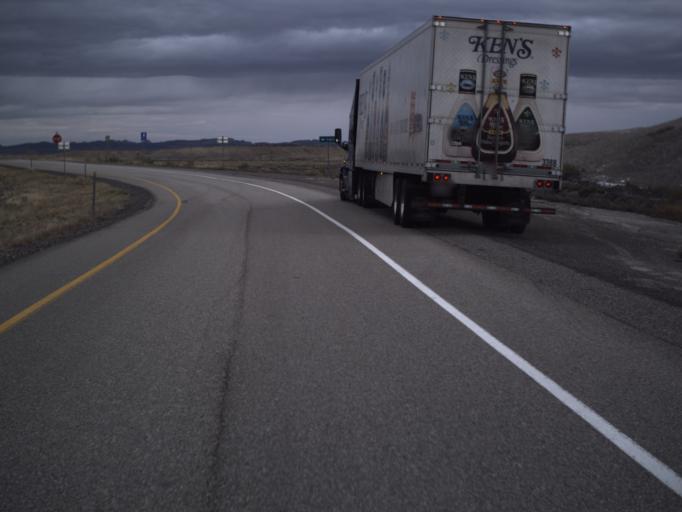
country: US
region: Utah
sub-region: Emery County
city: Ferron
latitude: 38.8102
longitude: -111.2127
